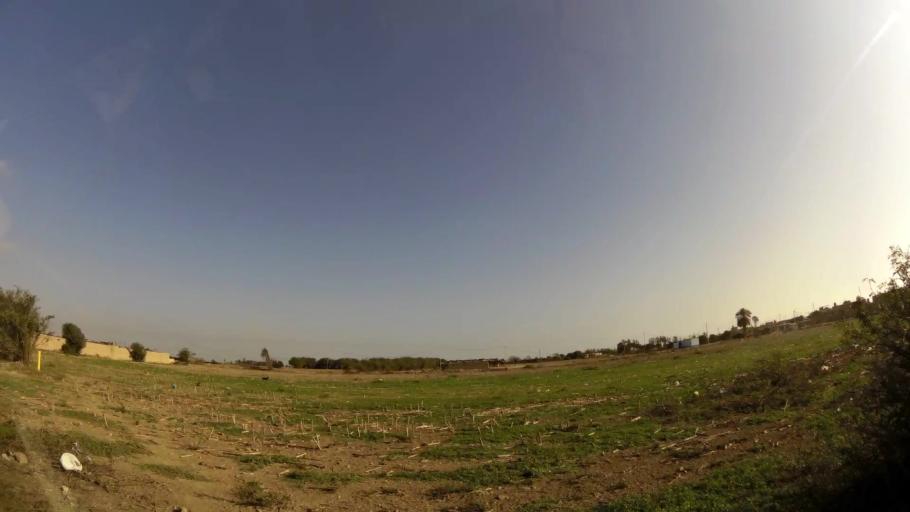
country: PE
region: Ica
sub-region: Provincia de Chincha
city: Chincha Baja
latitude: -13.4637
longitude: -76.1852
